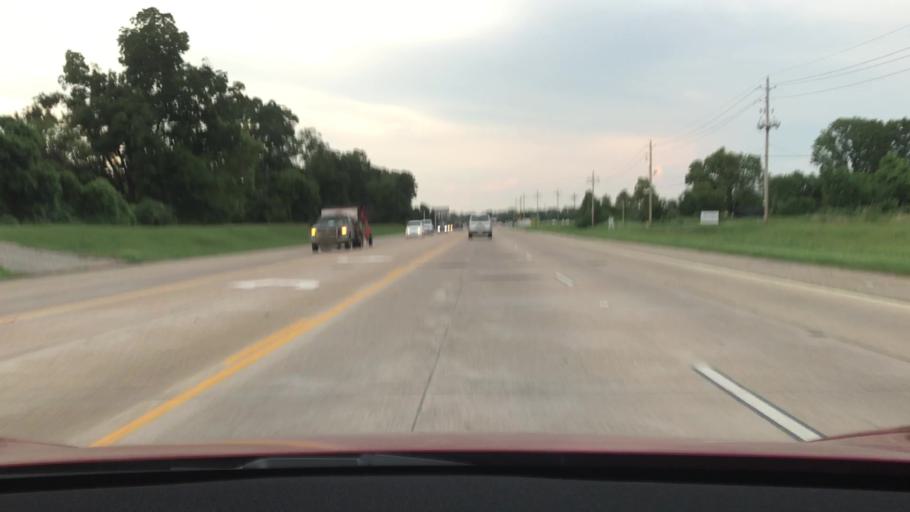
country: US
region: Louisiana
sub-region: Bossier Parish
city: Bossier City
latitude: 32.4538
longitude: -93.6934
